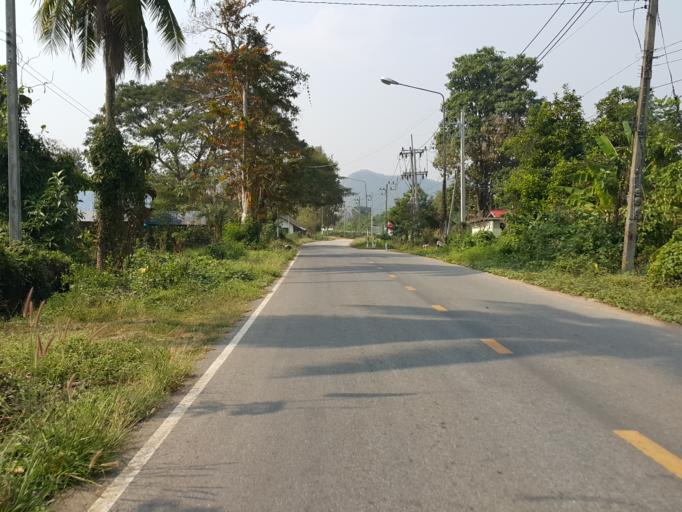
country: TH
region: Sukhothai
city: Thung Saliam
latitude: 17.3276
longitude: 99.5049
